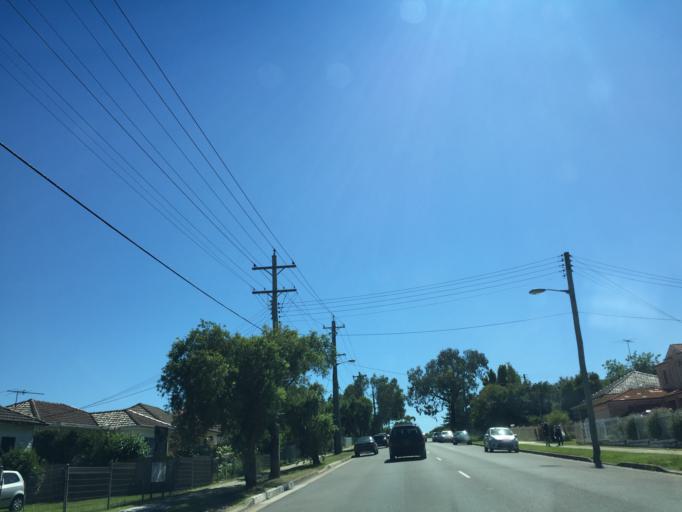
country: AU
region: New South Wales
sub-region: Blacktown
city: Blacktown
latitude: -33.7695
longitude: 150.8995
